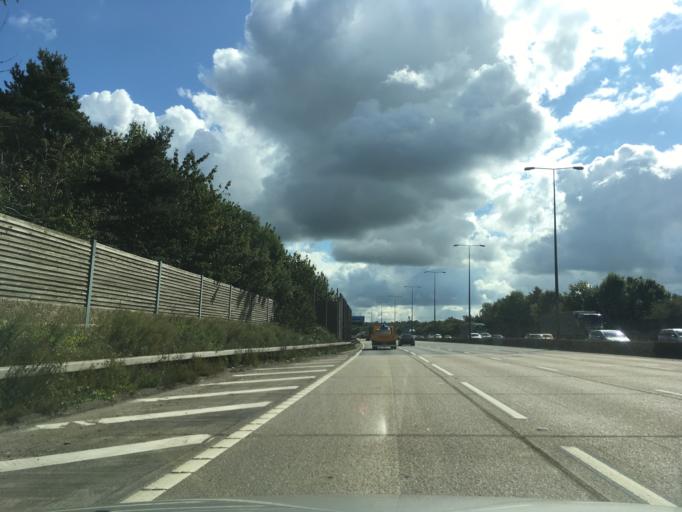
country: GB
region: England
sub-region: Surrey
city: Byfleet
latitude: 51.3287
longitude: -0.4772
